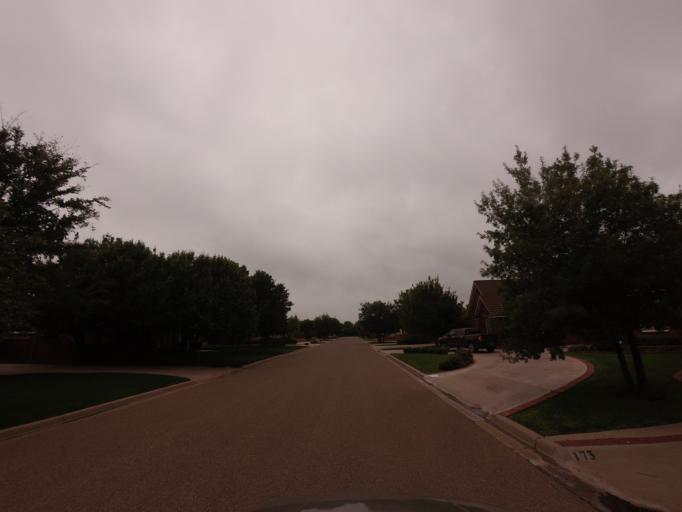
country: US
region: New Mexico
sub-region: Curry County
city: Clovis
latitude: 34.4290
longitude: -103.1827
